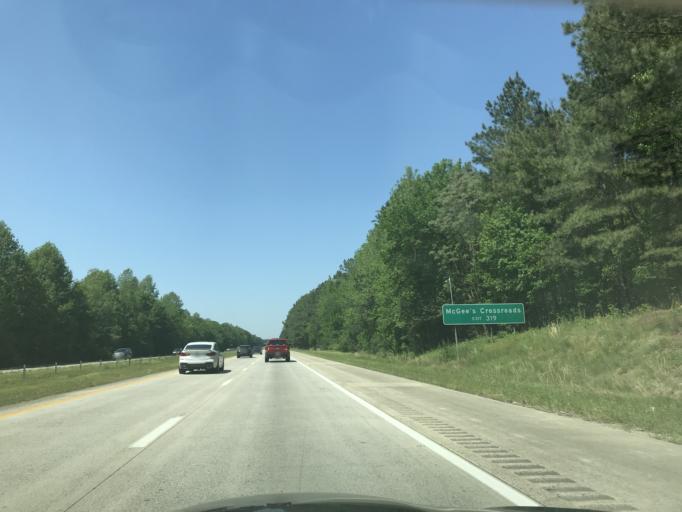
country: US
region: North Carolina
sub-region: Johnston County
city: Benson
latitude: 35.4943
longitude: -78.5529
